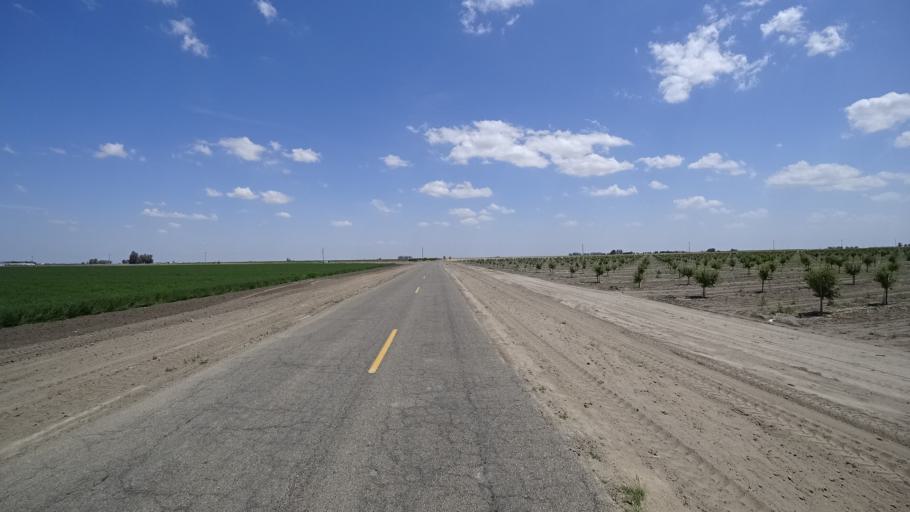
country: US
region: California
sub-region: Kings County
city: Stratford
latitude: 36.1823
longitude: -119.8012
